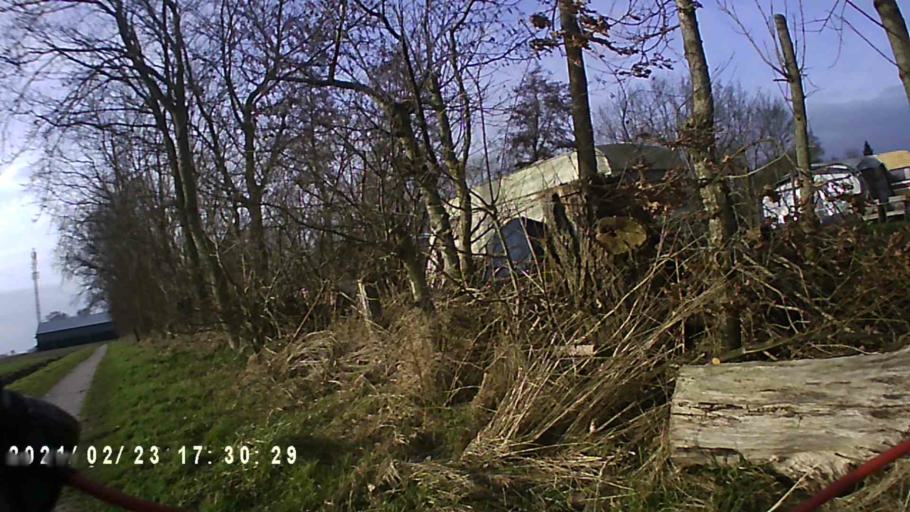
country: NL
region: Groningen
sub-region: Gemeente Winsum
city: Winsum
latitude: 53.3983
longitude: 6.4520
